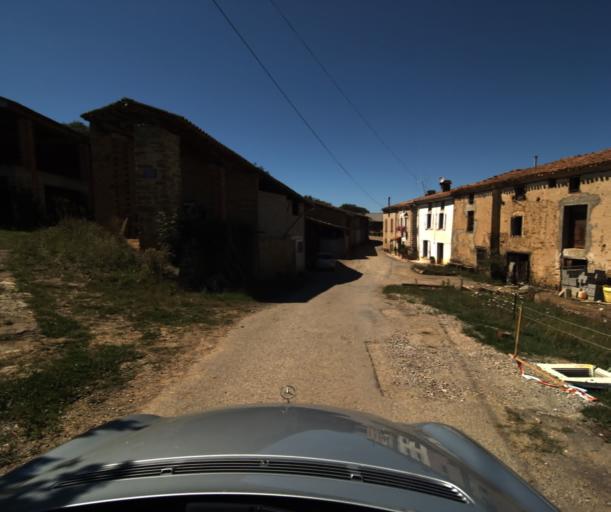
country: FR
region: Midi-Pyrenees
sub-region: Departement de l'Ariege
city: Belesta
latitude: 42.9626
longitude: 1.9315
